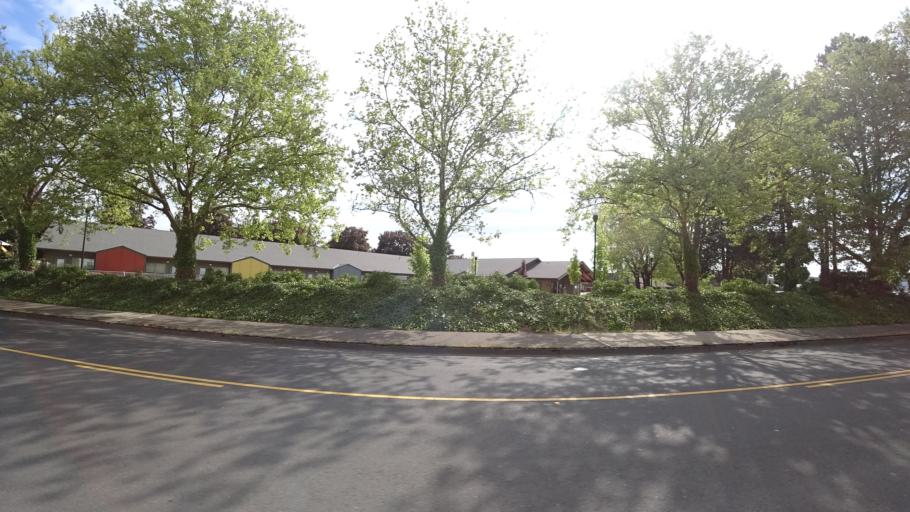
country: US
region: Oregon
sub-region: Washington County
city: Hillsboro
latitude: 45.5075
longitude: -122.9667
